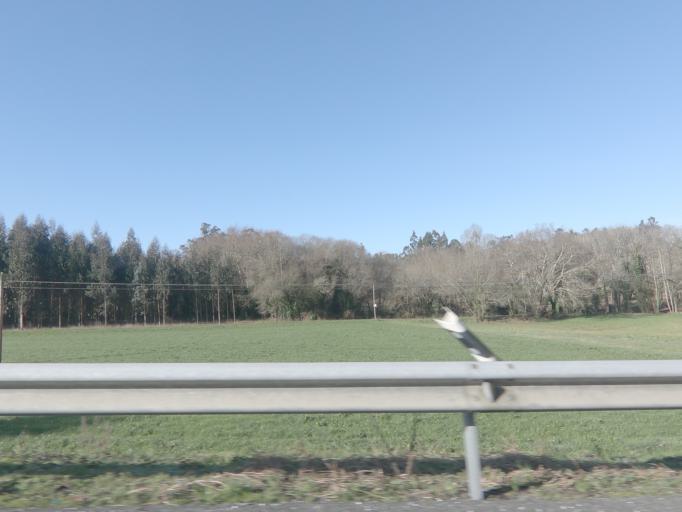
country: ES
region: Galicia
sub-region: Provincia da Coruna
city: Vedra
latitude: 42.8140
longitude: -8.4787
